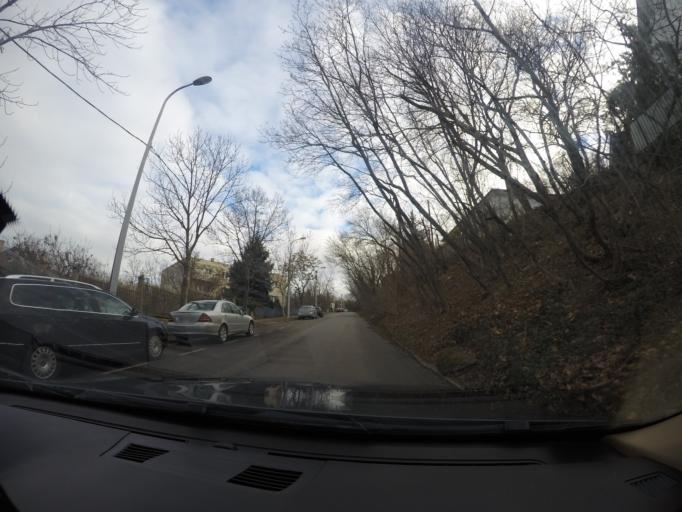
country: HU
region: Budapest
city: Budapest I. keruelet
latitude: 47.4878
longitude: 19.0371
